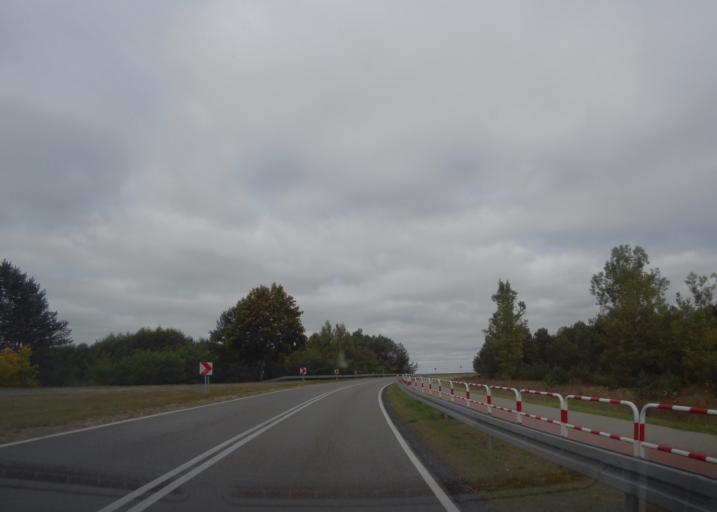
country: PL
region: Lublin Voivodeship
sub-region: Powiat wlodawski
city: Wlodawa
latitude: 51.5253
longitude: 23.5213
